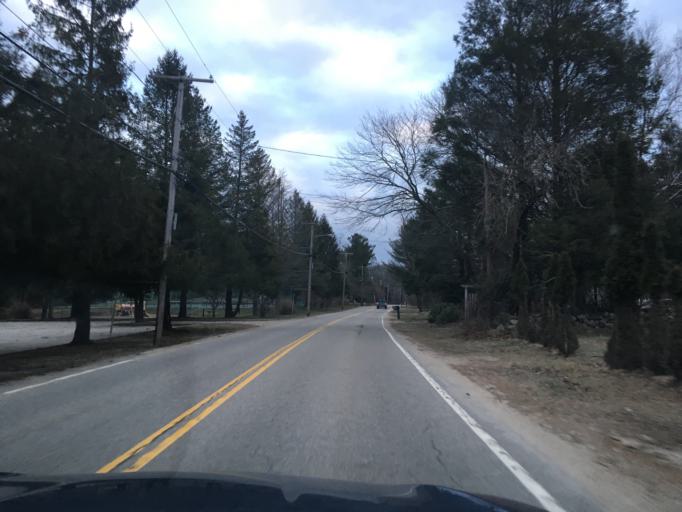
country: US
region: Rhode Island
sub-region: Washington County
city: Exeter
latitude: 41.6235
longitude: -71.5211
